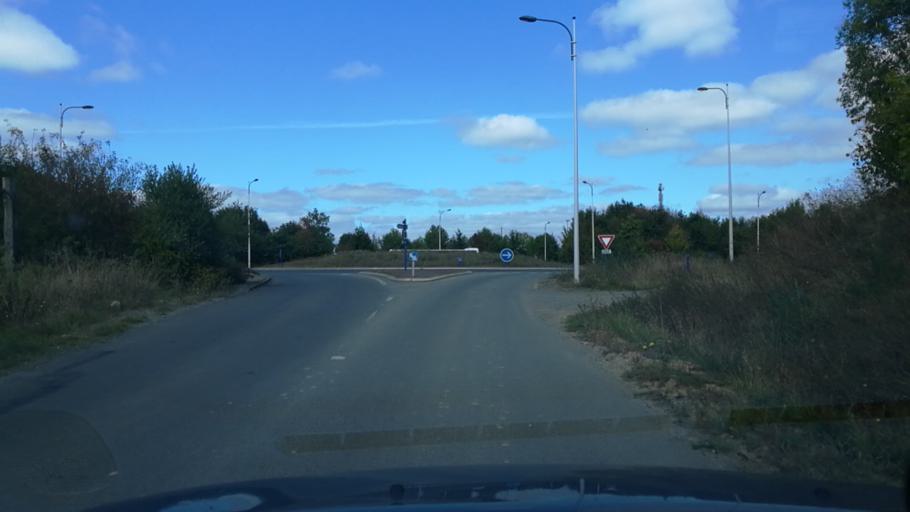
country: FR
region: Brittany
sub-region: Departement d'Ille-et-Vilaine
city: Montgermont
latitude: 48.1496
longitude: -1.7222
